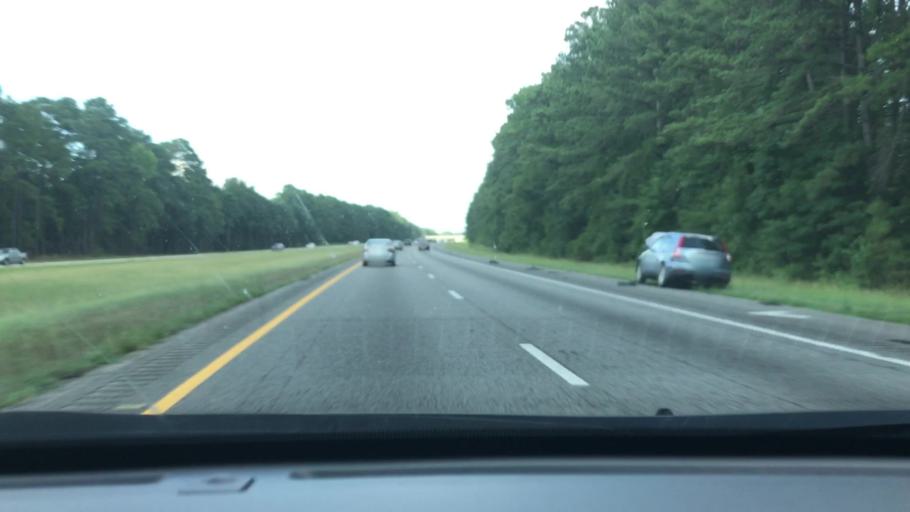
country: US
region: South Carolina
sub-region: Dillon County
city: Latta
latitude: 34.4034
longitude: -79.4432
